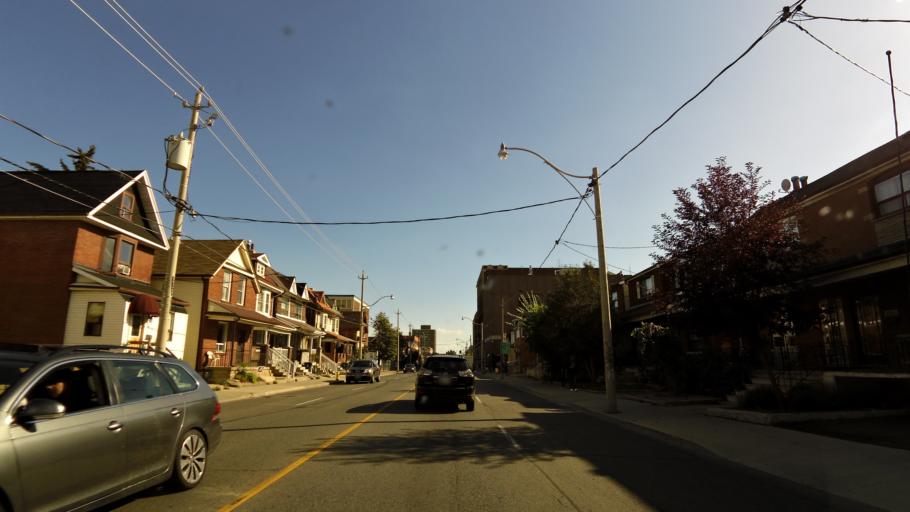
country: CA
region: Ontario
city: Toronto
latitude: 43.6619
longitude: -79.4362
